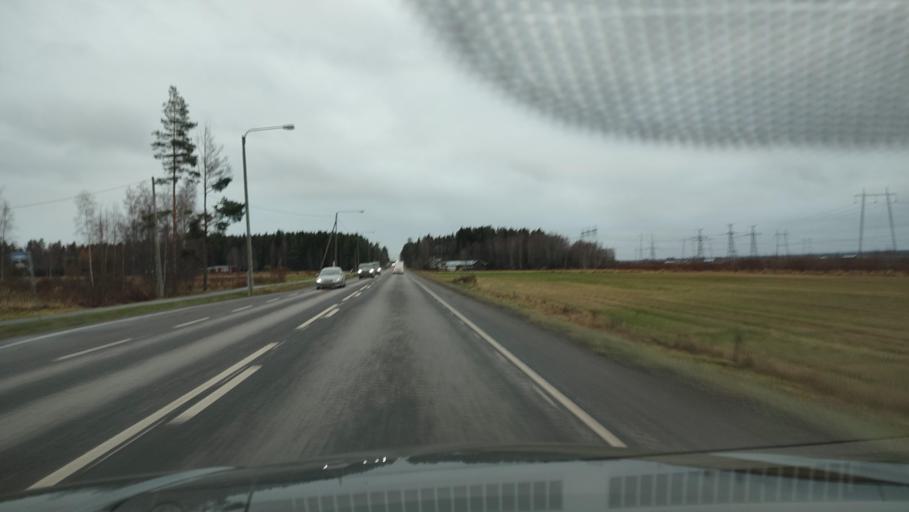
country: FI
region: Southern Ostrobothnia
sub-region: Seinaejoki
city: Seinaejoki
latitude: 62.7890
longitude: 22.7258
